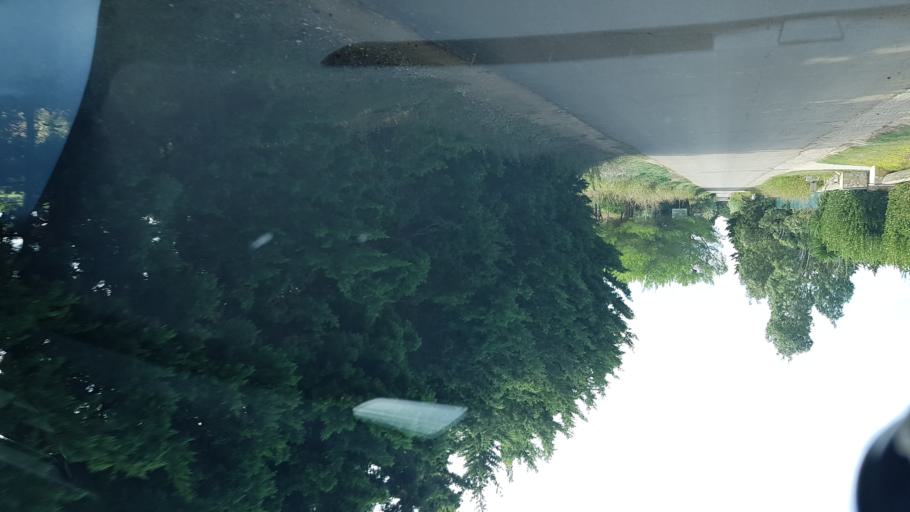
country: IT
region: Apulia
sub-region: Provincia di Lecce
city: Borgagne
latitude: 40.2292
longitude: 18.4467
